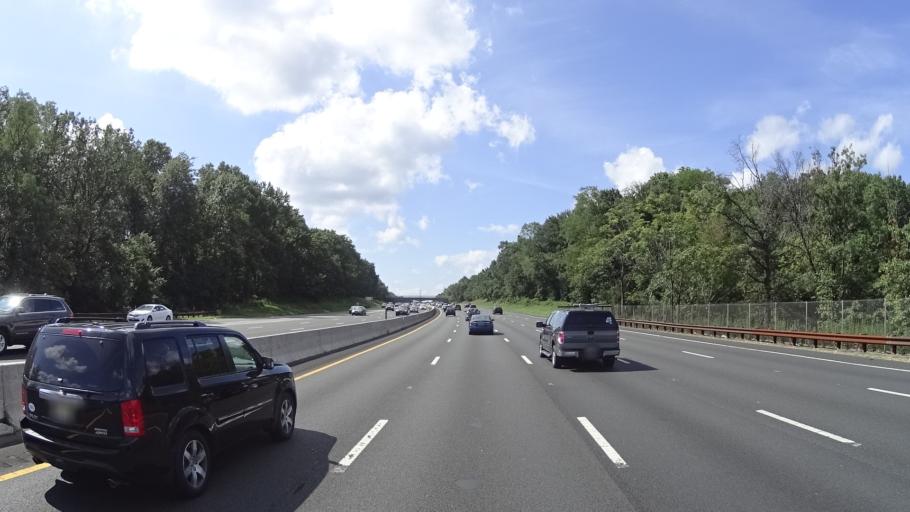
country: US
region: New Jersey
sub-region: Union County
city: Clark
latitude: 40.6195
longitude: -74.3105
